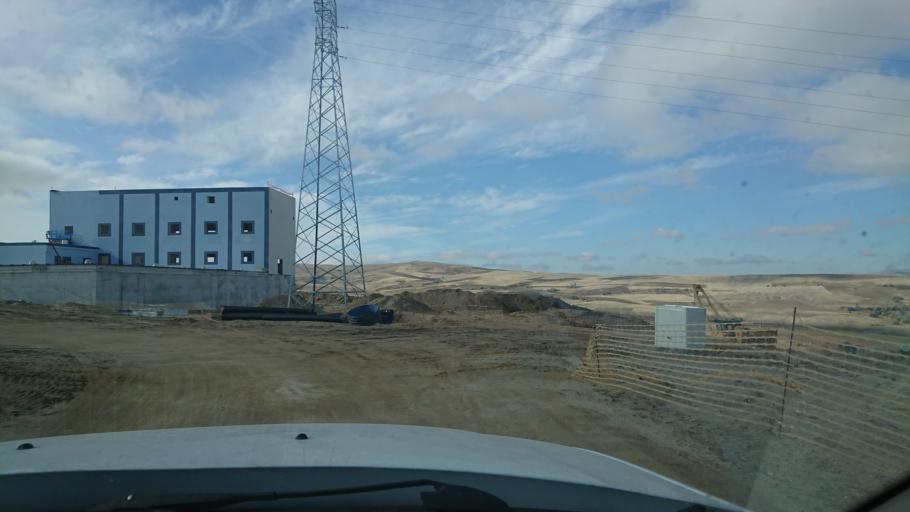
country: TR
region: Aksaray
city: Agacoren
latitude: 38.8467
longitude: 33.9447
